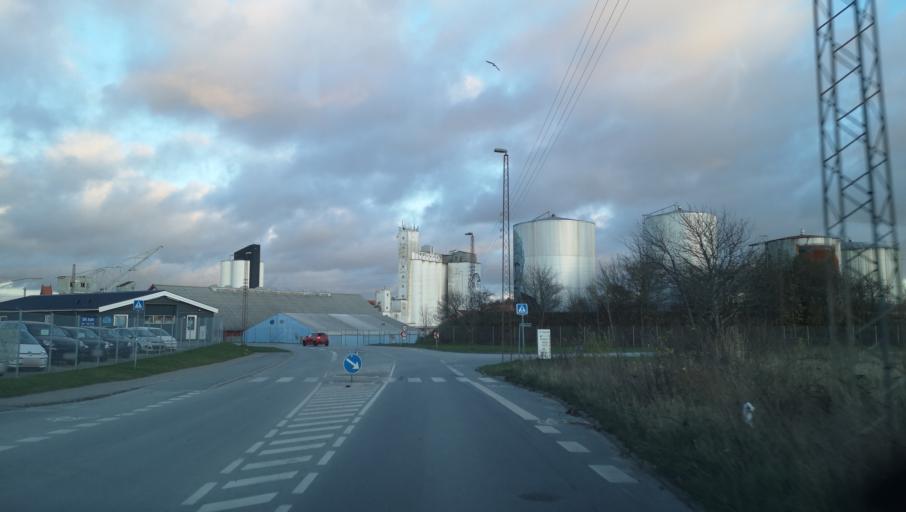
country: DK
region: Zealand
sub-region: Naestved Kommune
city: Naestved
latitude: 55.2255
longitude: 11.7512
